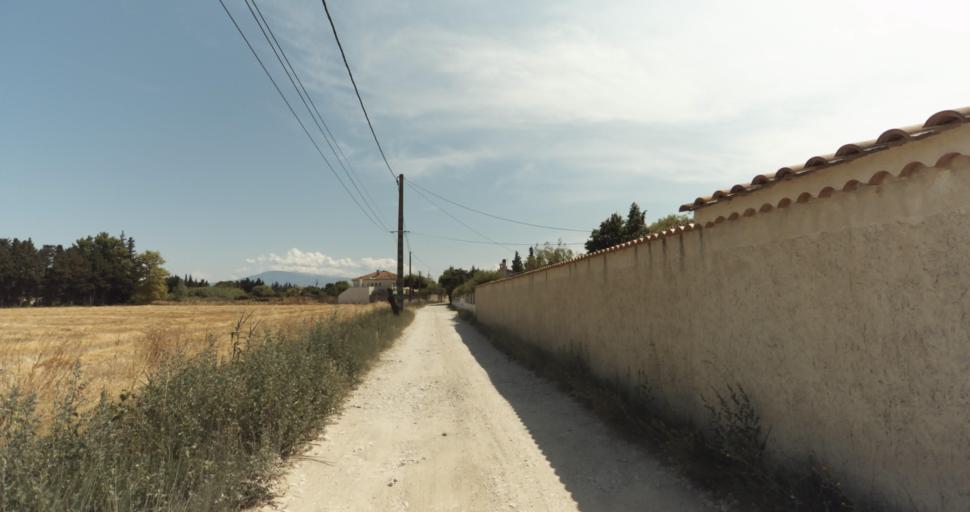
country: FR
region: Provence-Alpes-Cote d'Azur
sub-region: Departement du Vaucluse
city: Monteux
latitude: 44.0211
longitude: 4.9888
